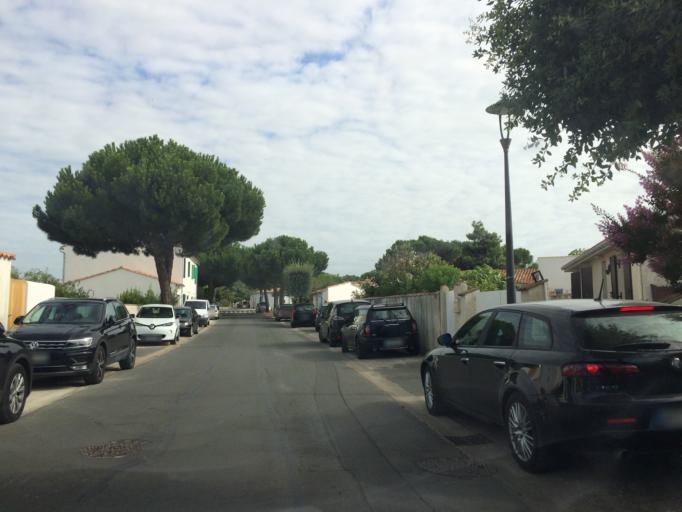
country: FR
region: Poitou-Charentes
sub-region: Departement de la Charente-Maritime
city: La Flotte
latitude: 46.1877
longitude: -1.3342
